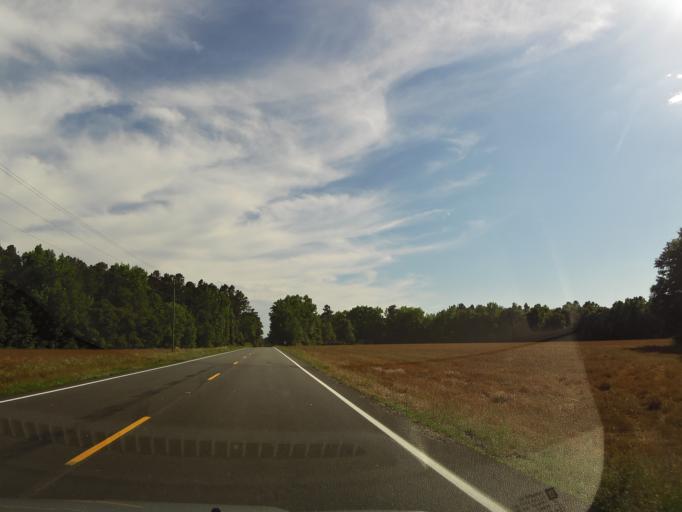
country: US
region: South Carolina
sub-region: Allendale County
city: Fairfax
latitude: 32.9773
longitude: -81.2295
